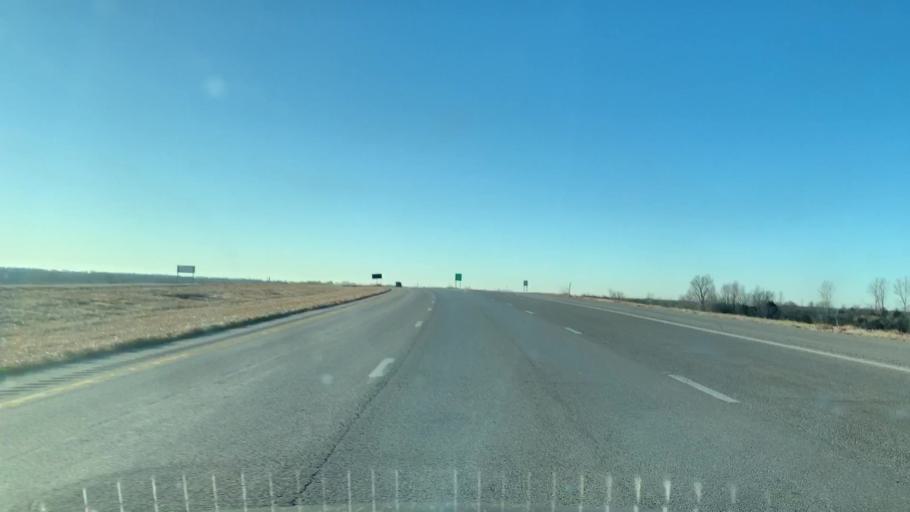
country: US
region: Kansas
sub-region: Bourbon County
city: Fort Scott
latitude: 37.7711
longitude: -94.7062
